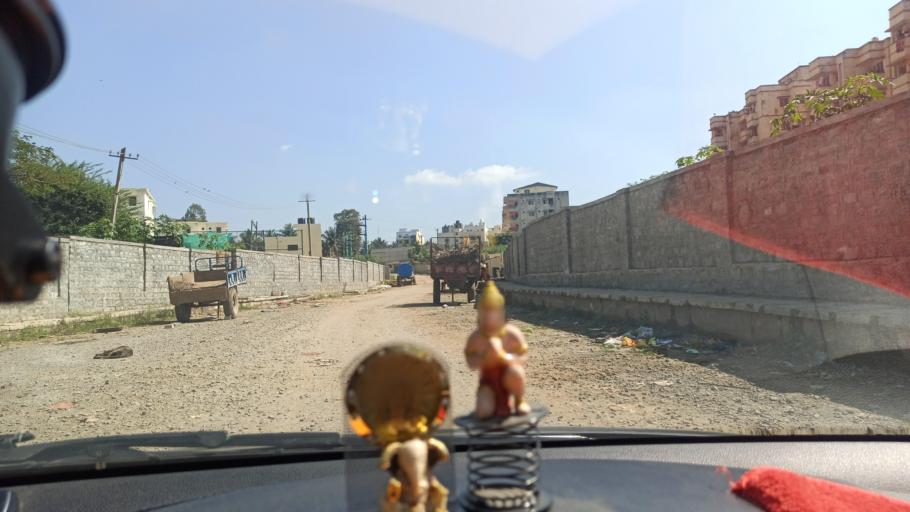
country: IN
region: Karnataka
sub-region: Bangalore Urban
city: Bangalore
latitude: 12.9614
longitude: 77.6978
